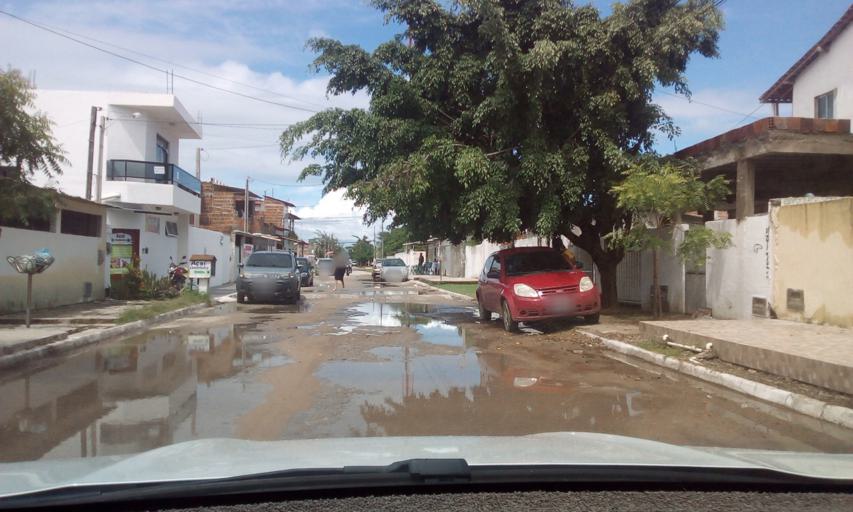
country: BR
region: Paraiba
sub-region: Cabedelo
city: Cabedelo
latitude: -7.0051
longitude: -34.8328
